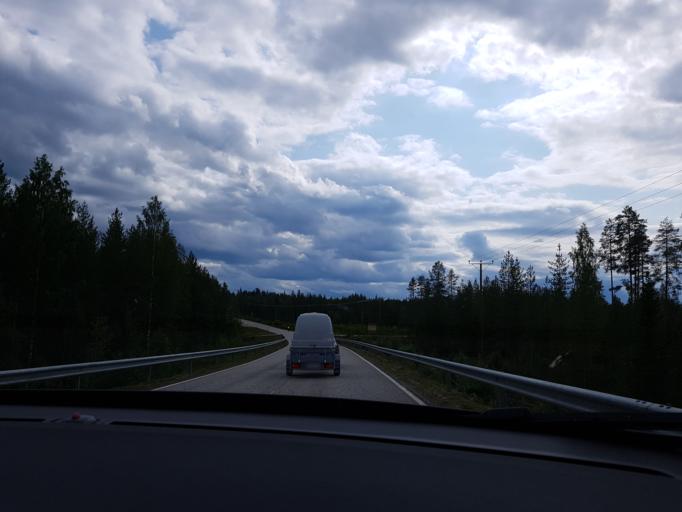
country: FI
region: Kainuu
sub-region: Kehys-Kainuu
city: Kuhmo
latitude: 64.2497
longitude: 29.8080
